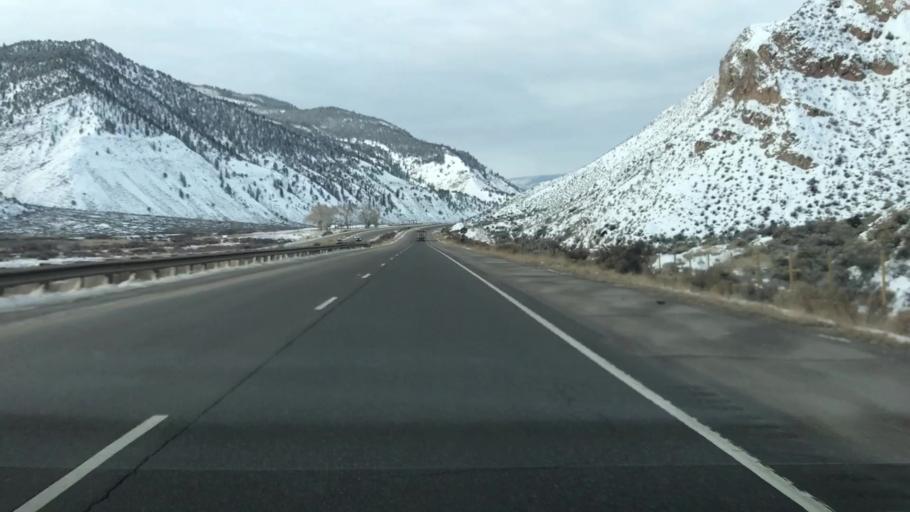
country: US
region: Colorado
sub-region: Eagle County
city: Gypsum
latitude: 39.6468
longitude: -107.0184
